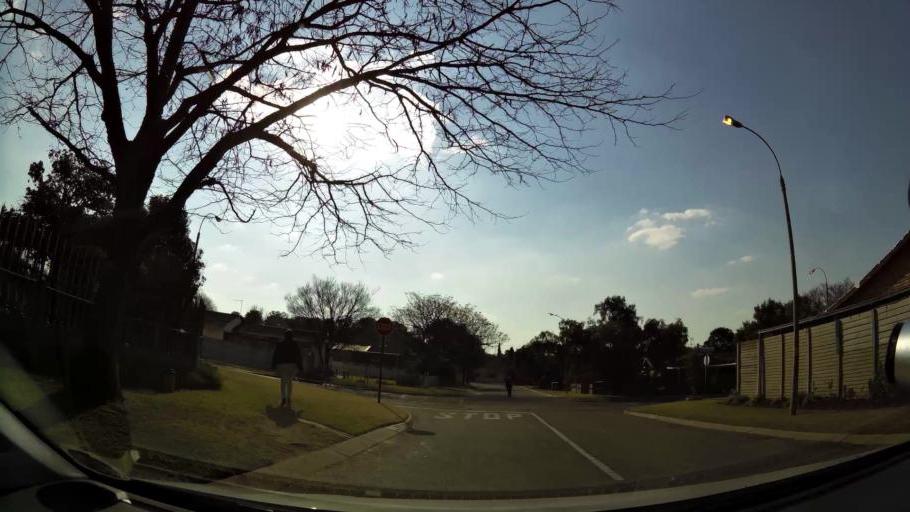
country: ZA
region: Gauteng
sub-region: City of Johannesburg Metropolitan Municipality
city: Modderfontein
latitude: -26.0871
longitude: 28.1980
